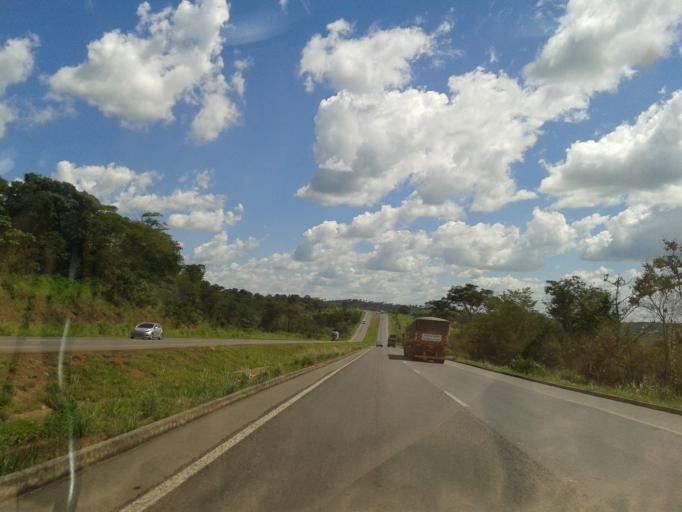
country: BR
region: Goias
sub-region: Piracanjuba
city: Piracanjuba
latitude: -17.3511
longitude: -49.2483
